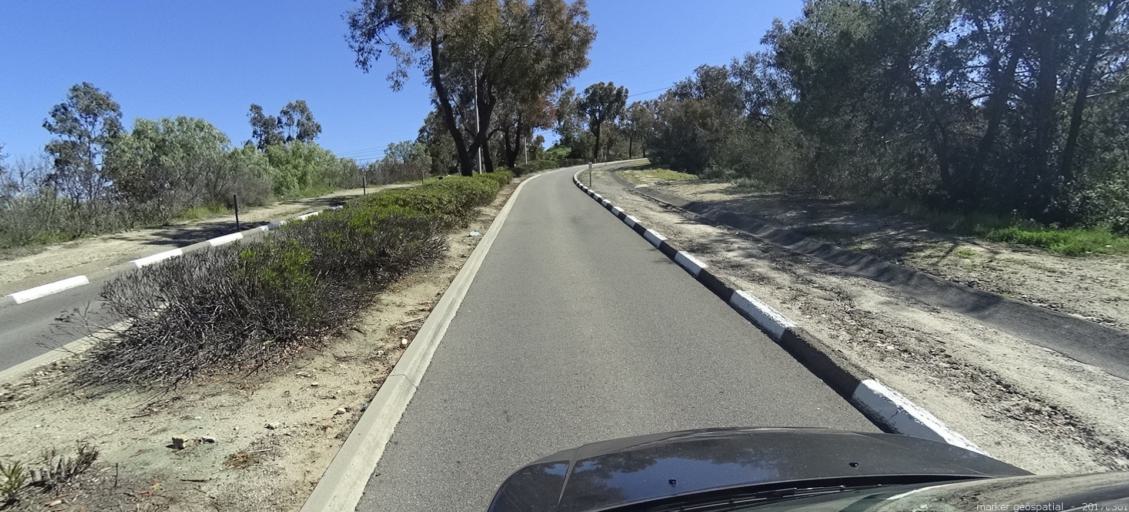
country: US
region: California
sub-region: Orange County
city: Villa Park
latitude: 33.8496
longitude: -117.7595
